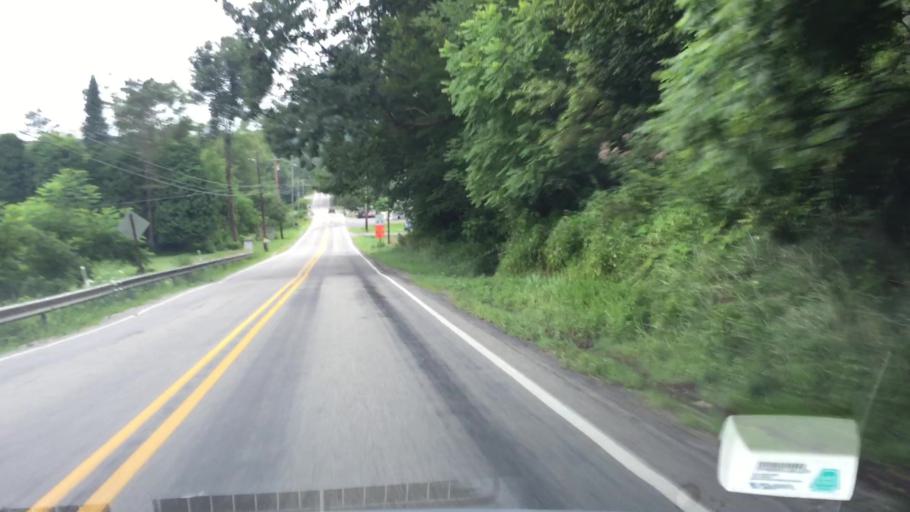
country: US
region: Pennsylvania
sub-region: Allegheny County
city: Curtisville
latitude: 40.6764
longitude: -79.8291
